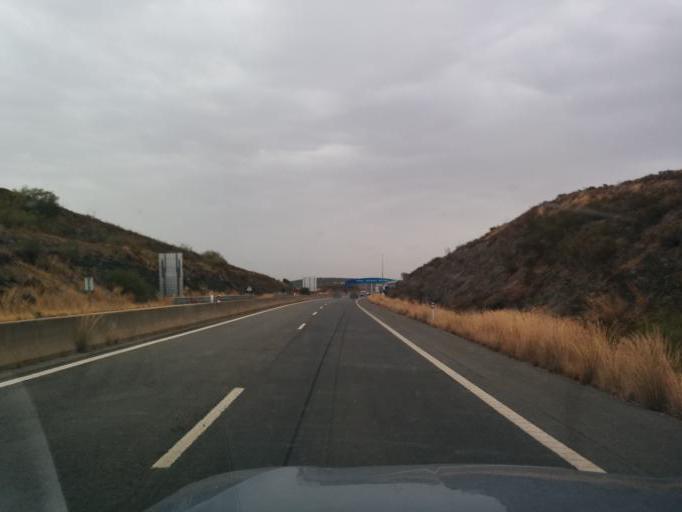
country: PT
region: Faro
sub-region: Castro Marim
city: Castro Marim
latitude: 37.2370
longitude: -7.4347
